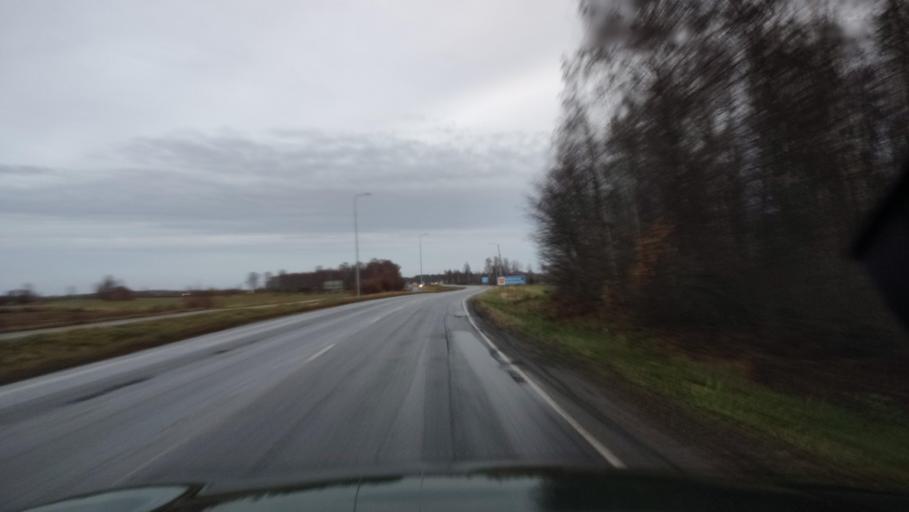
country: FI
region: Ostrobothnia
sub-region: Vaasa
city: Ristinummi
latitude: 63.0440
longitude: 21.7360
